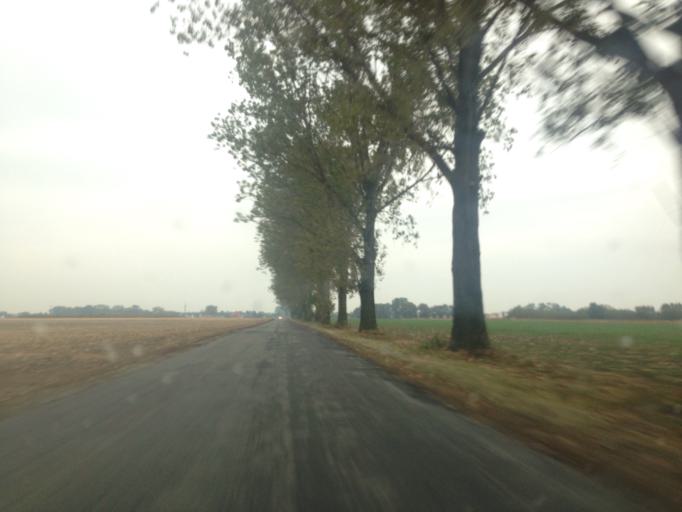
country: PL
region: Greater Poland Voivodeship
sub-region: Powiat poznanski
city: Kleszczewo
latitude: 52.3537
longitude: 17.1434
